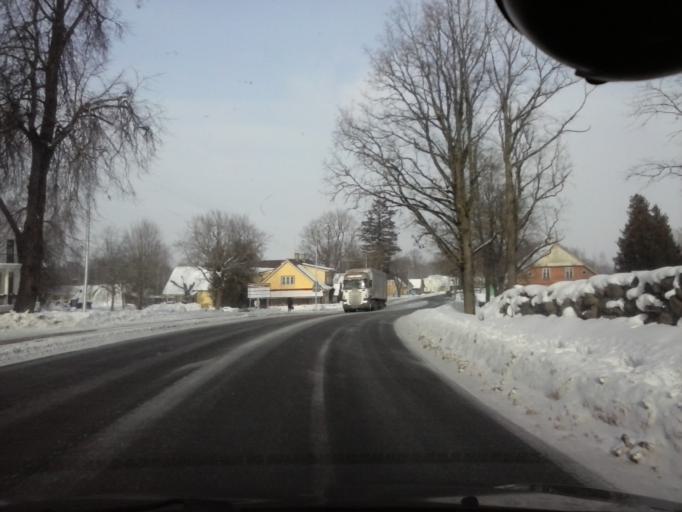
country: EE
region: Viljandimaa
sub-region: Abja vald
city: Abja-Paluoja
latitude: 58.3256
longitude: 25.3057
